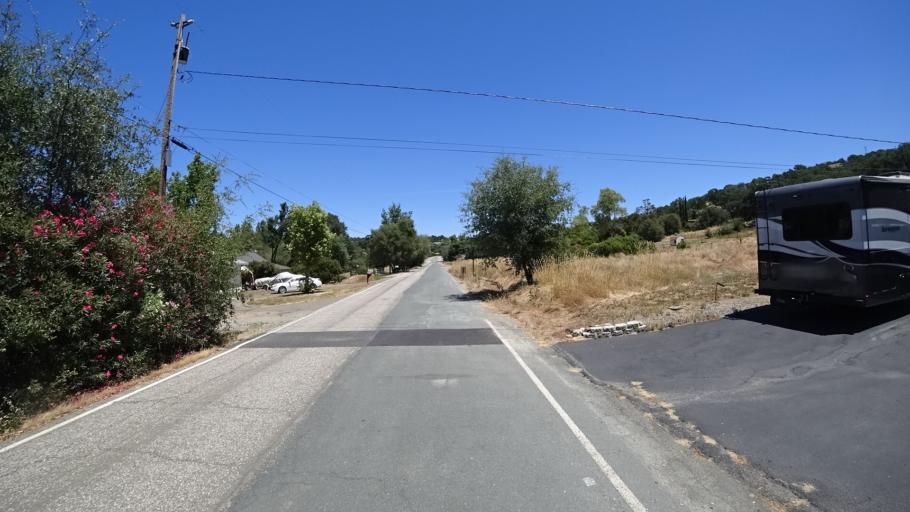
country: US
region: California
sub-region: Calaveras County
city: Rancho Calaveras
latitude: 38.1557
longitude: -120.8467
